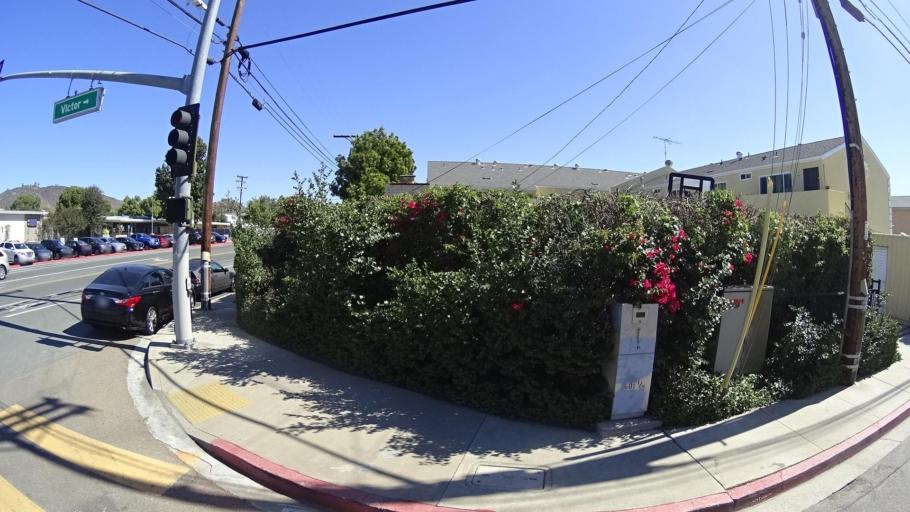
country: US
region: California
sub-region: San Diego County
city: Bostonia
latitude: 32.8132
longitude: -116.9553
